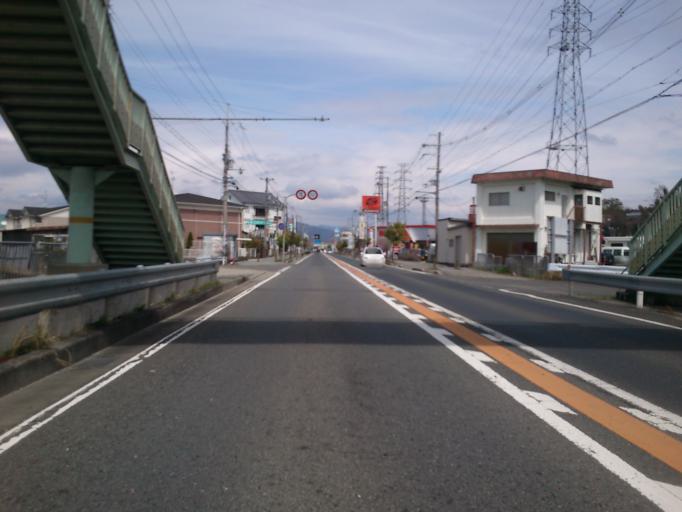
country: JP
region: Nara
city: Nara-shi
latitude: 34.7243
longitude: 135.8182
